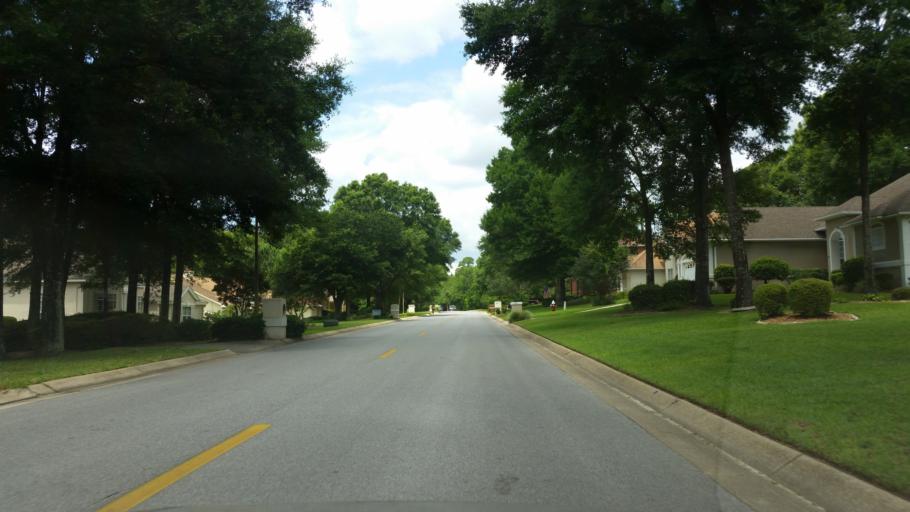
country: US
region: Florida
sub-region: Escambia County
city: Ensley
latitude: 30.4803
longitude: -87.2804
